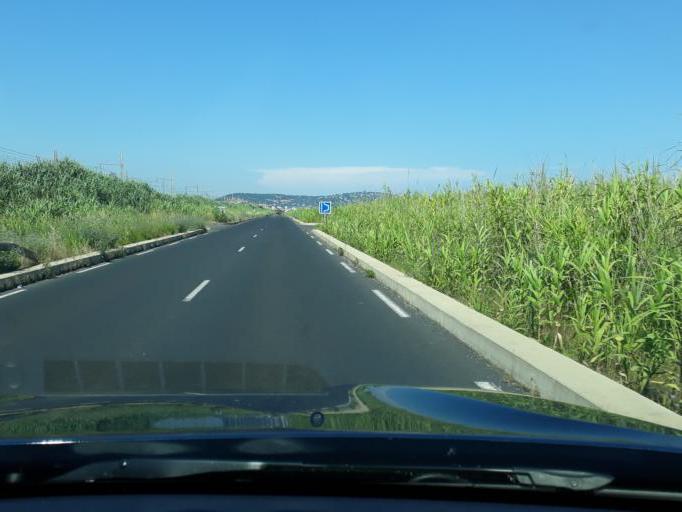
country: FR
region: Languedoc-Roussillon
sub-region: Departement de l'Herault
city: Meze
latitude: 43.3718
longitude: 3.6222
